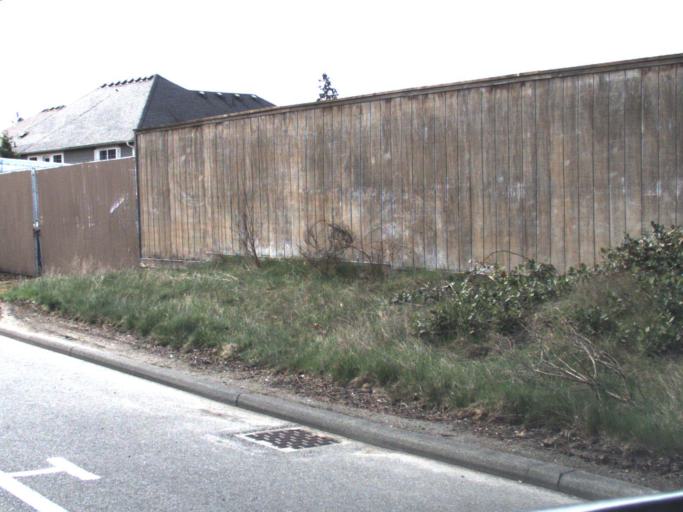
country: US
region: Washington
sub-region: Pierce County
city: Edgewood
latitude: 47.2659
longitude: -122.3009
